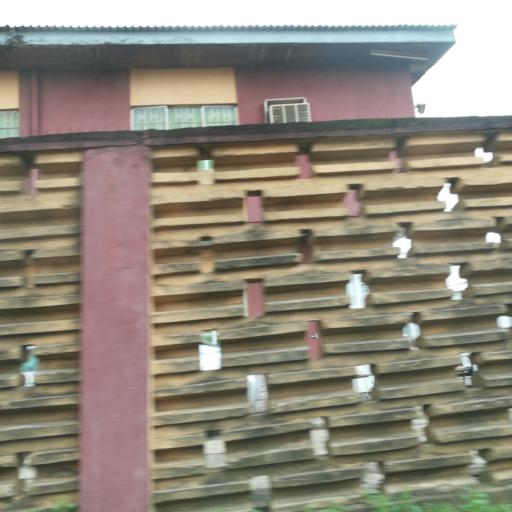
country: NG
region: Lagos
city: Agege
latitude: 6.5993
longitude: 3.2961
